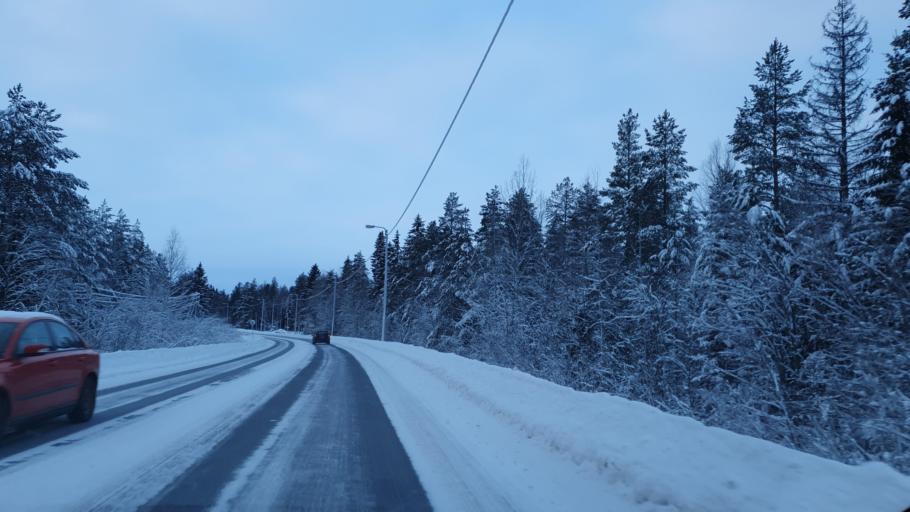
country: FI
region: Northern Ostrobothnia
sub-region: Oulu
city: Haukipudas
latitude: 65.2006
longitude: 25.4034
